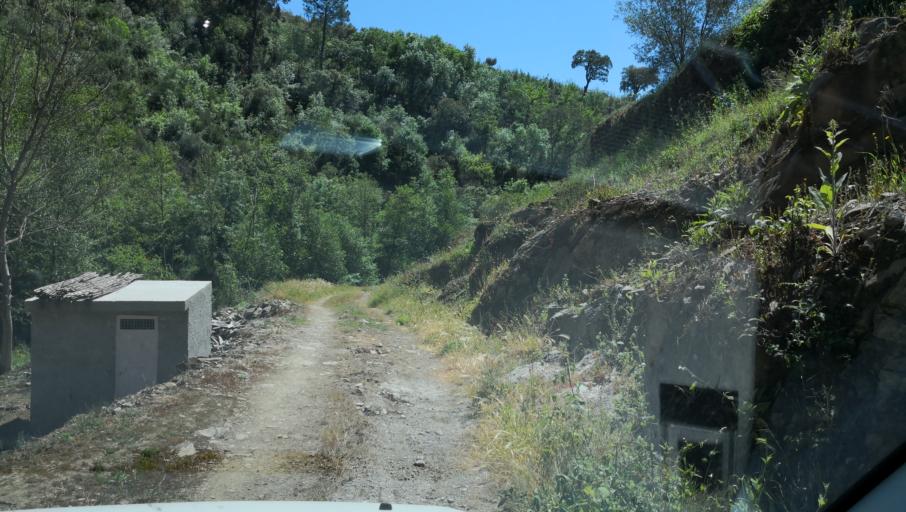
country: PT
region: Vila Real
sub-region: Vila Real
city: Vila Real
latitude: 41.2300
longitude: -7.7161
